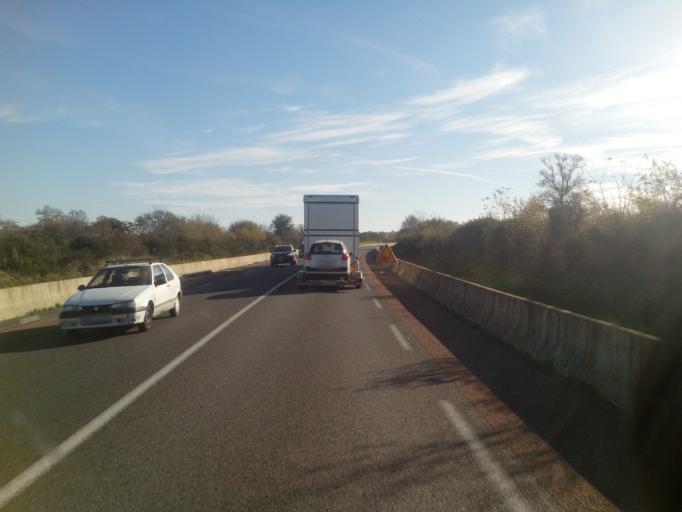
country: FR
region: Limousin
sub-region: Departement de la Haute-Vienne
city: Bellac
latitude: 46.1335
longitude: 1.0665
